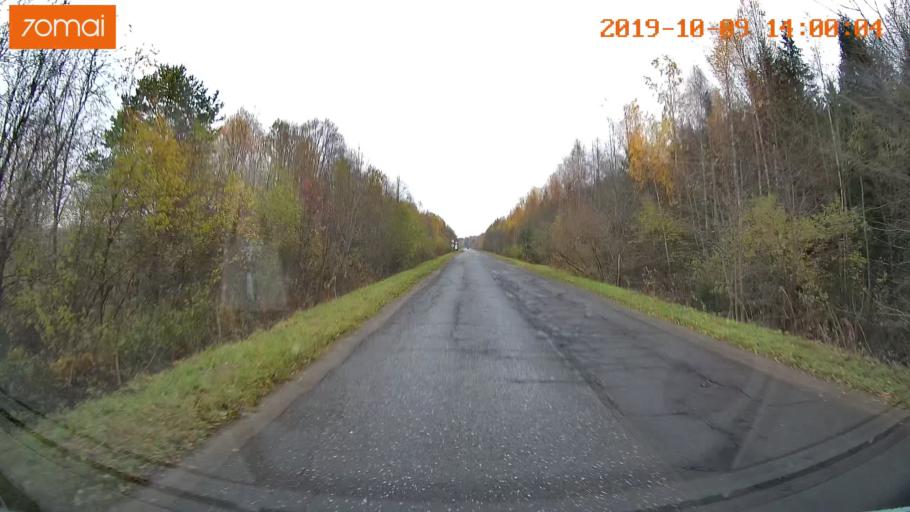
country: RU
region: Kostroma
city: Buy
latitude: 58.4379
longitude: 41.3311
